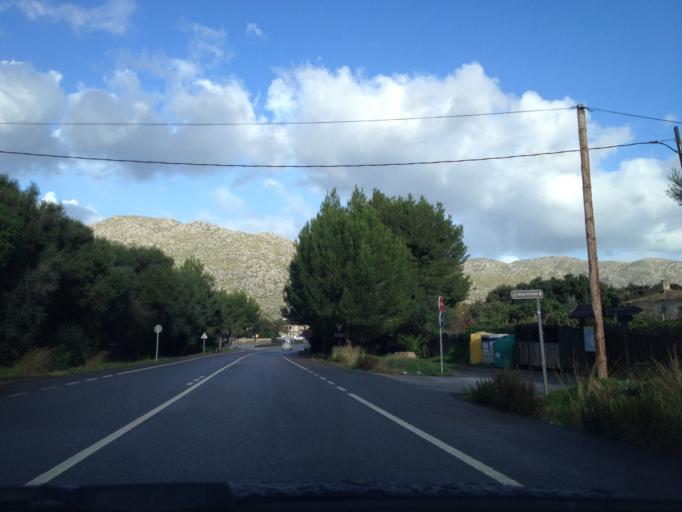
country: ES
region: Balearic Islands
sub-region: Illes Balears
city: Pollenca
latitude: 39.8824
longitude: 3.0235
